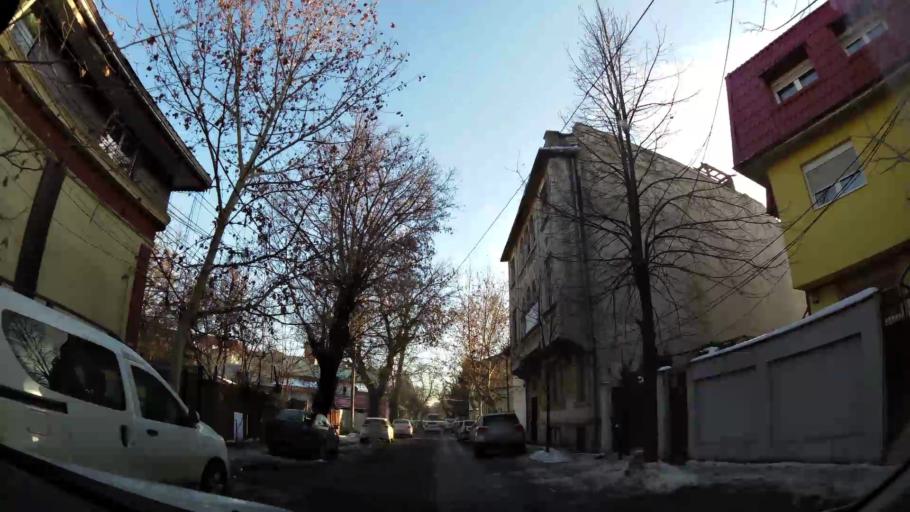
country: RO
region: Bucuresti
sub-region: Municipiul Bucuresti
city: Bucharest
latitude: 44.4390
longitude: 26.1290
